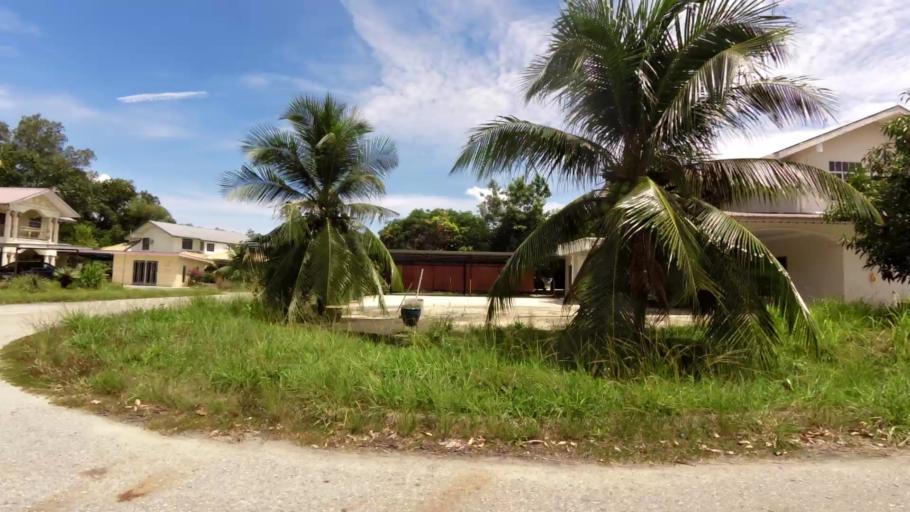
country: BN
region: Brunei and Muara
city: Bandar Seri Begawan
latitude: 4.9596
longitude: 114.8981
